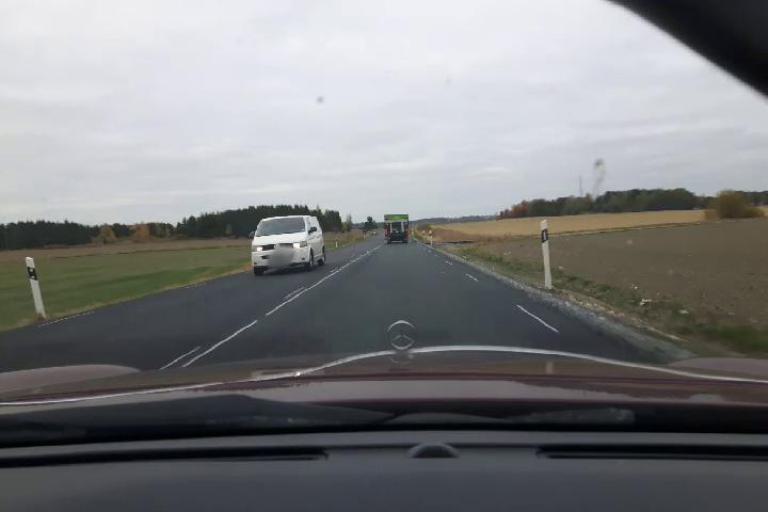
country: SE
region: Uppsala
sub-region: Enkopings Kommun
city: Enkoping
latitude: 59.6111
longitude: 17.0275
